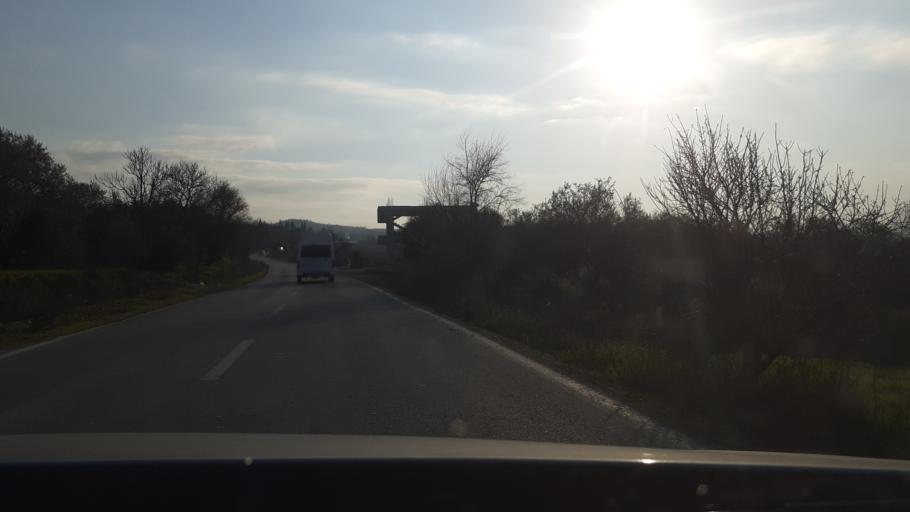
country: TR
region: Hatay
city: Oymakli
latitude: 36.1181
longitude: 36.3044
